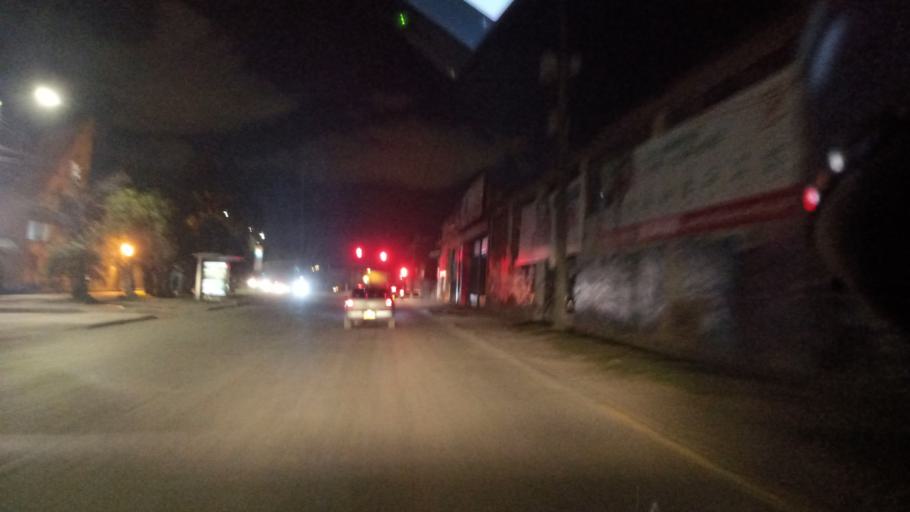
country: CO
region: Cundinamarca
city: Funza
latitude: 4.6839
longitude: -74.1564
